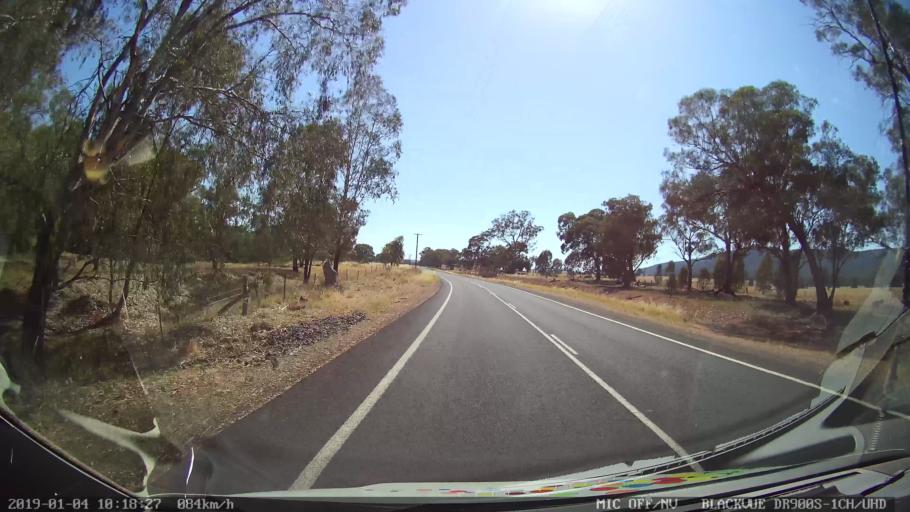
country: AU
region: New South Wales
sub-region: Cabonne
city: Canowindra
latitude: -33.3820
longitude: 148.4668
